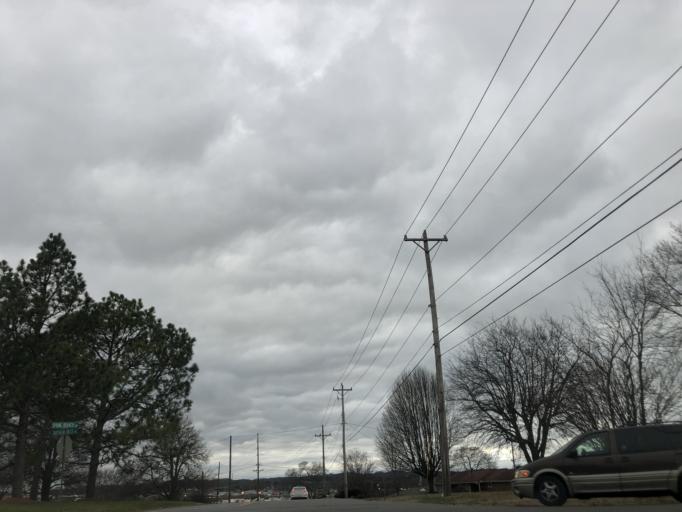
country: US
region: Tennessee
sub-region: Davidson County
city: Goodlettsville
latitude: 36.2948
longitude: -86.6913
